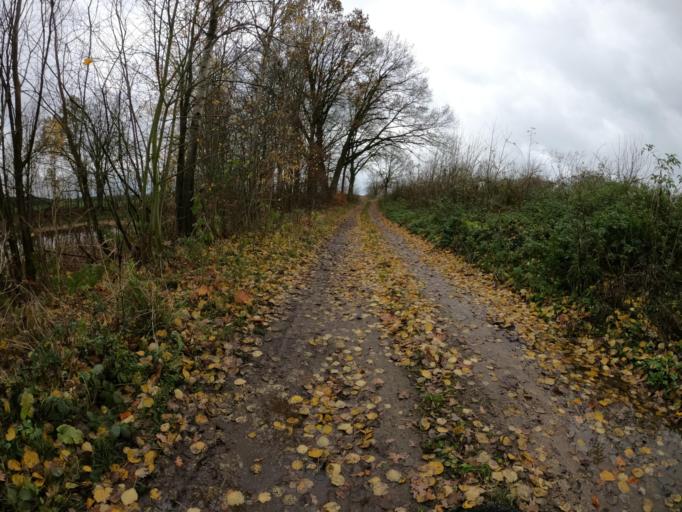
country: PL
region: West Pomeranian Voivodeship
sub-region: Powiat walecki
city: Tuczno
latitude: 53.2610
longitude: 16.2335
